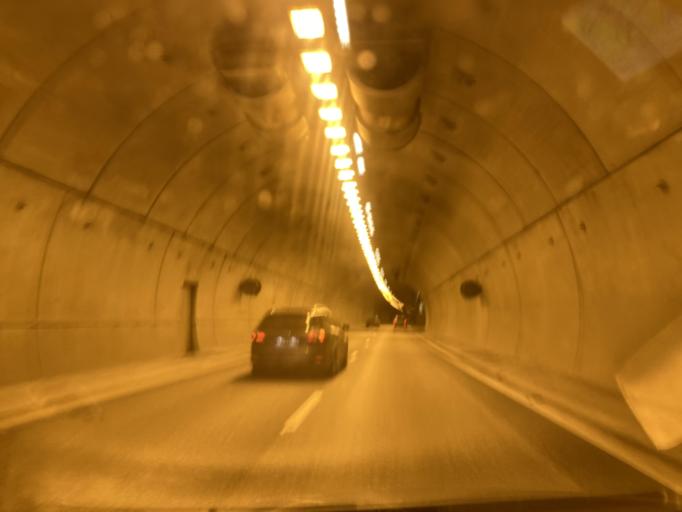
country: NO
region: Hedmark
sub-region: Stange
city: Stange
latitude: 60.5788
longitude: 11.2750
